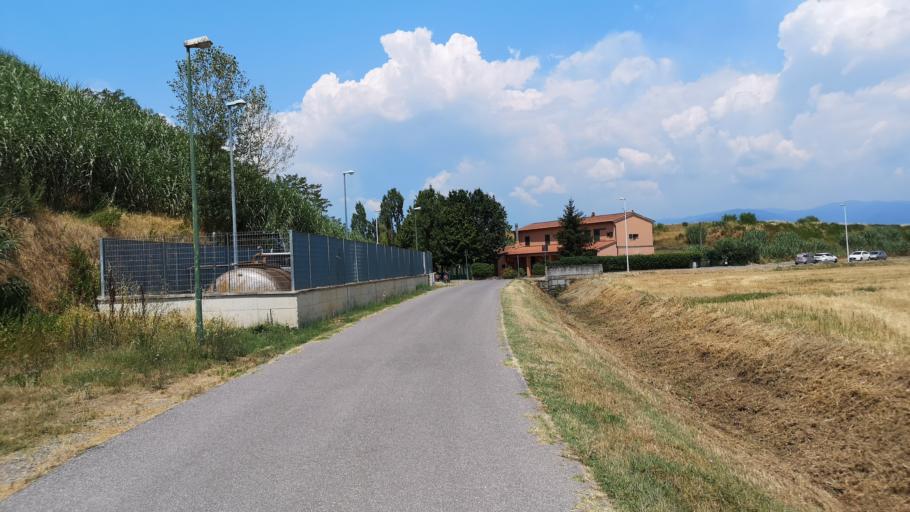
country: IT
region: Tuscany
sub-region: Provincia di Pistoia
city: Catena
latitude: 43.8512
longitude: 11.0333
